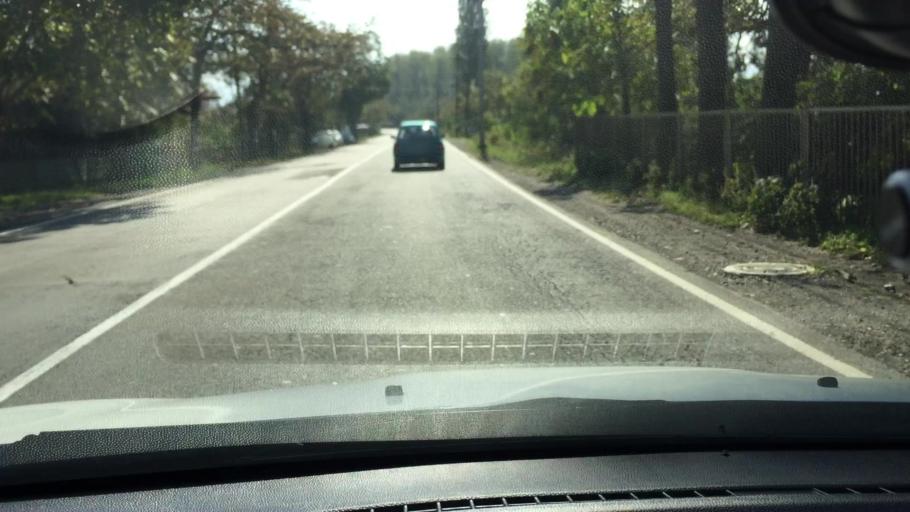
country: GE
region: Guria
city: Urek'i
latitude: 42.0305
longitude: 41.7466
